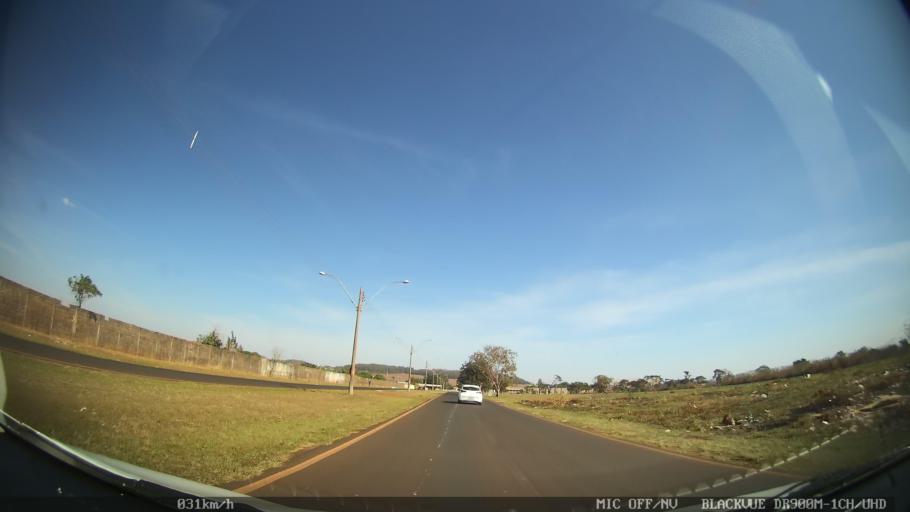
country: BR
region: Sao Paulo
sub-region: Ribeirao Preto
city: Ribeirao Preto
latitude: -21.1463
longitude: -47.7703
